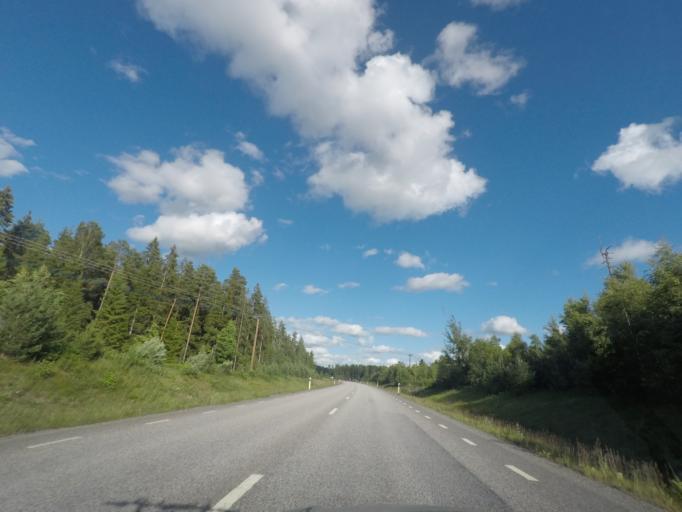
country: SE
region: OErebro
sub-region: Lindesbergs Kommun
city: Frovi
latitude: 59.4603
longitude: 15.4364
